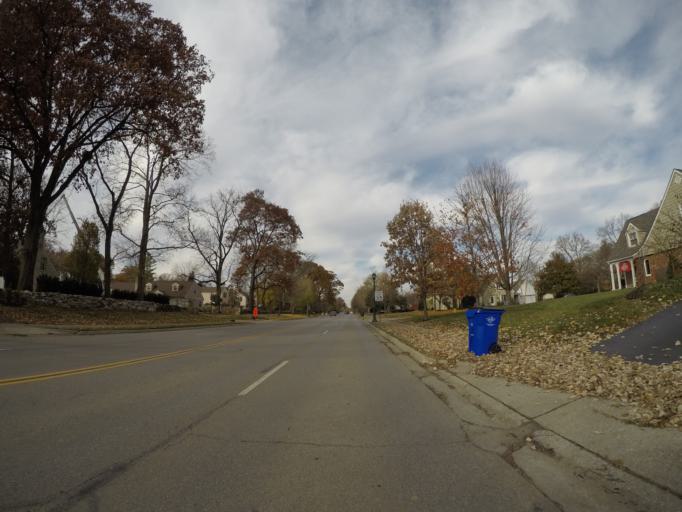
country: US
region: Ohio
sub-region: Franklin County
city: Upper Arlington
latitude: 40.0076
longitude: -83.0627
